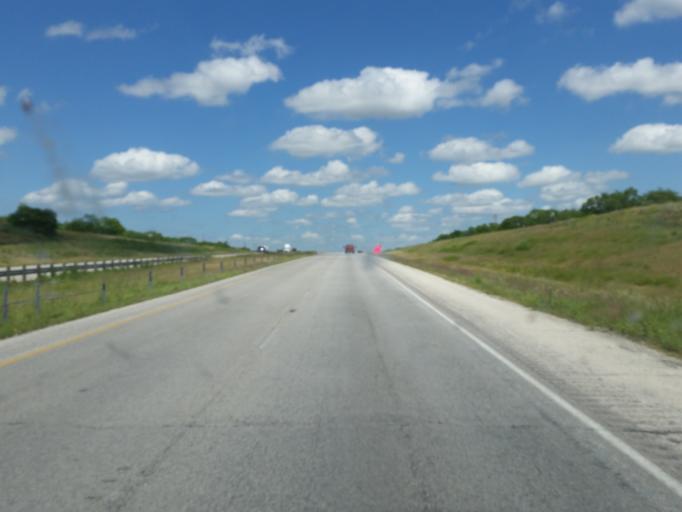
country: US
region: Texas
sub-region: Callahan County
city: Baird
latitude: 32.3808
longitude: -99.2697
